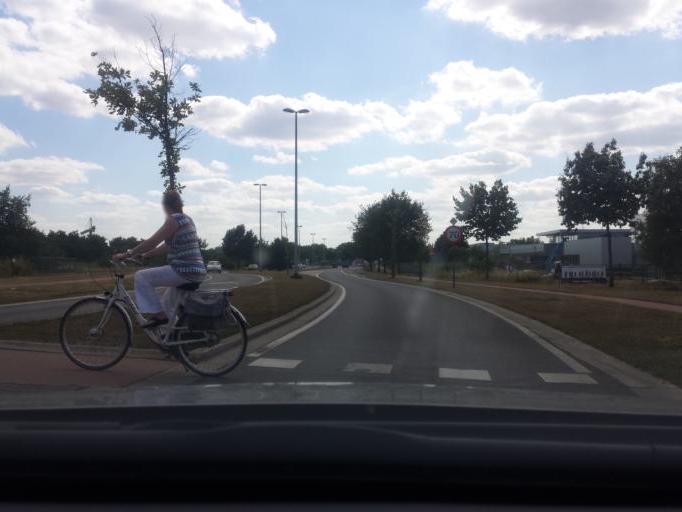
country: BE
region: Flanders
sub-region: Provincie Limburg
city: Beringen
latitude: 51.0569
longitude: 5.2220
